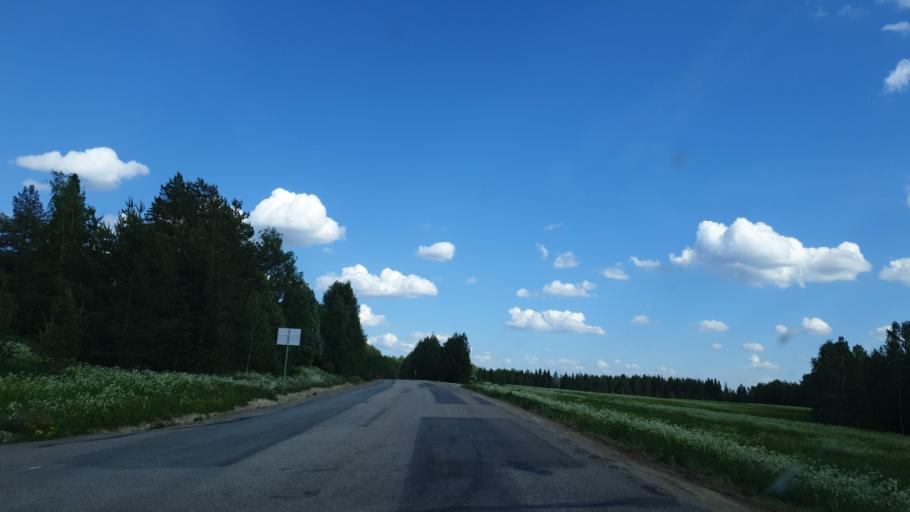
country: SE
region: Norrbotten
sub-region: Alvsbyns Kommun
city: AElvsbyn
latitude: 65.8539
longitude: 20.4370
